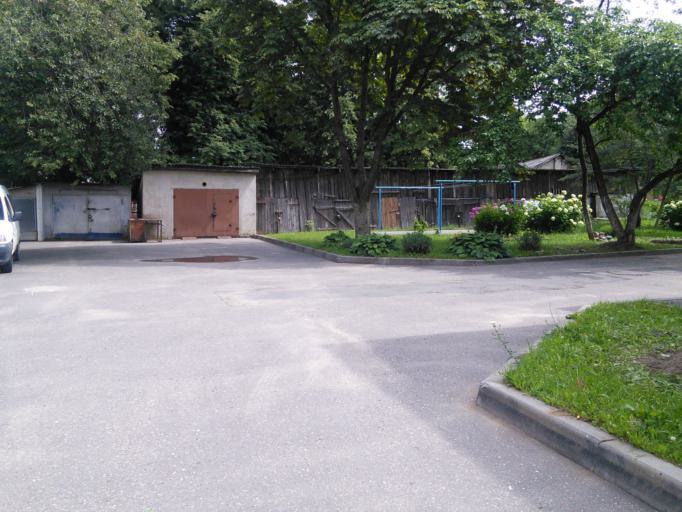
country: BY
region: Minsk
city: Maladzyechna
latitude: 54.3046
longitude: 26.8270
